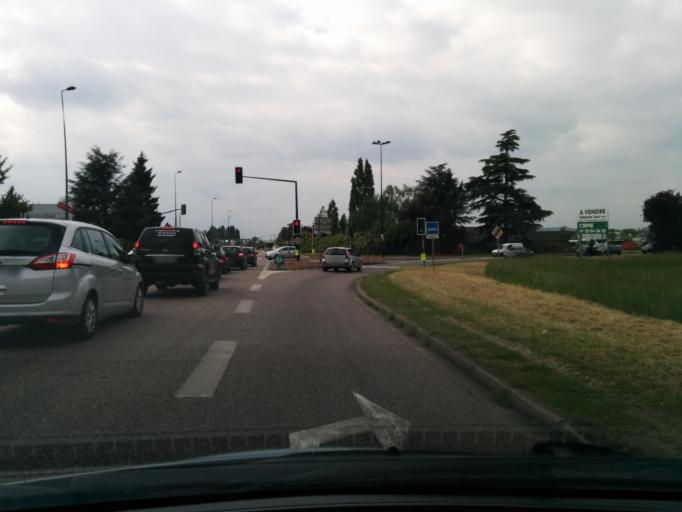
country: FR
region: Ile-de-France
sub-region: Departement des Yvelines
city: Epone
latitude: 48.9600
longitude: 1.8125
